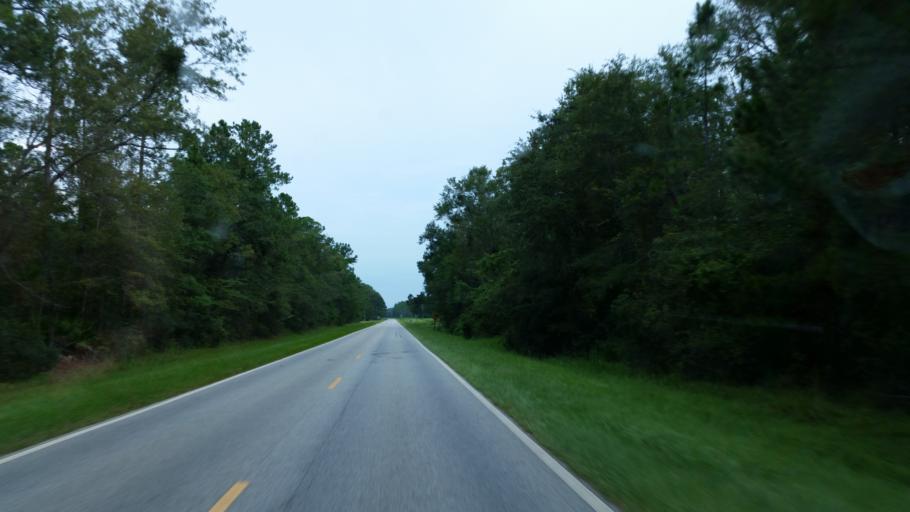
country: US
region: Georgia
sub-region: Lowndes County
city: Valdosta
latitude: 30.7513
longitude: -83.3081
